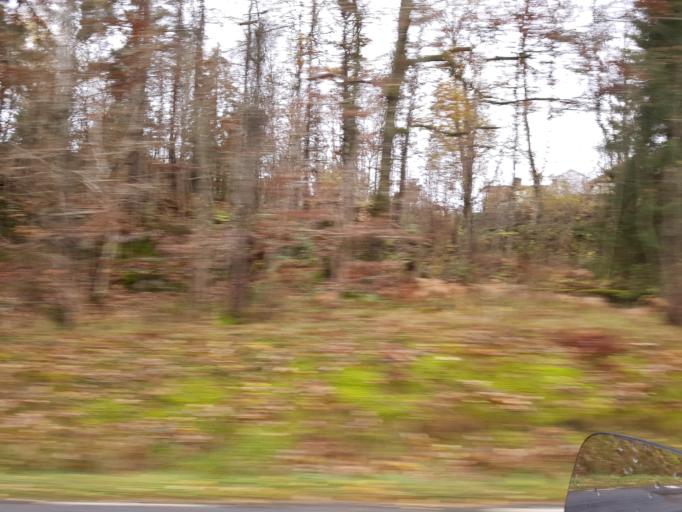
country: SE
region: Vaestra Goetaland
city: Svanesund
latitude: 58.1468
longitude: 11.8046
